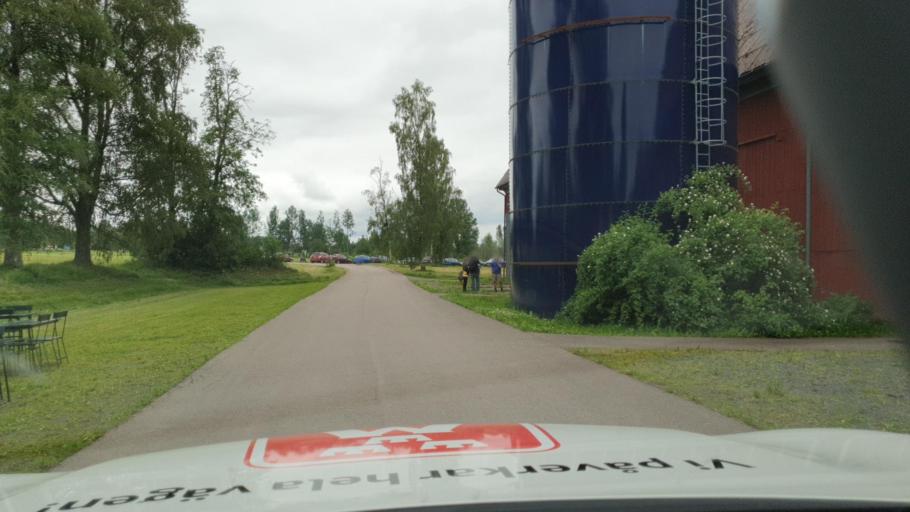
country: SE
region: Vaermland
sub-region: Sunne Kommun
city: Sunne
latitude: 59.8012
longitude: 13.1268
